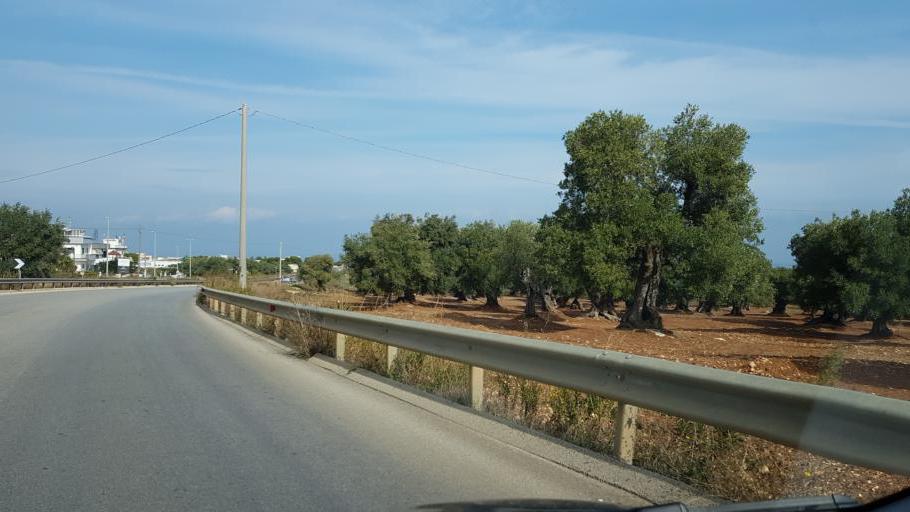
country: IT
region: Apulia
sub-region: Provincia di Brindisi
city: Ostuni
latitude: 40.7478
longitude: 17.5819
